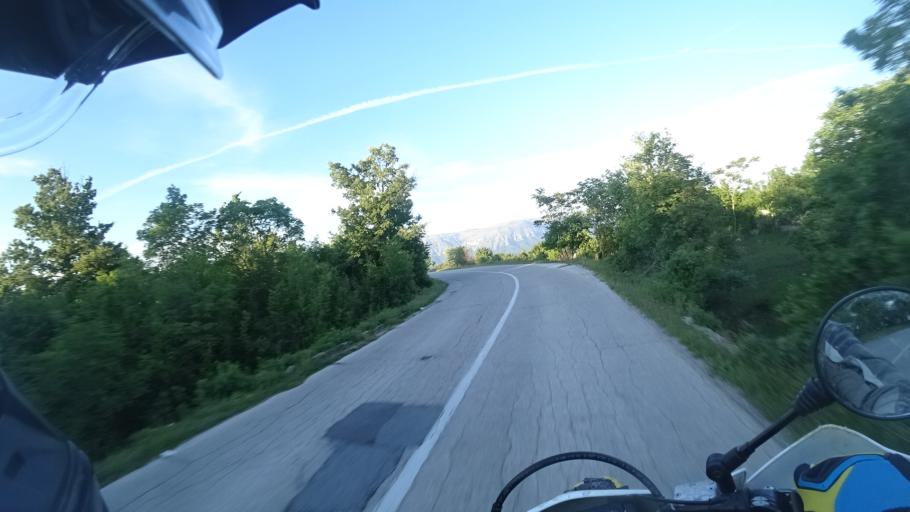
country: HR
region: Sibensko-Kniniska
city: Drnis
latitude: 43.8987
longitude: 16.3899
